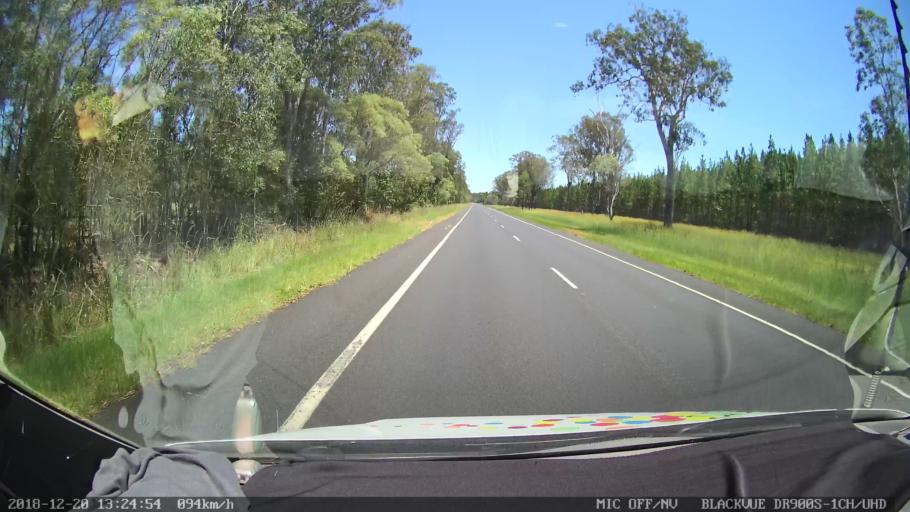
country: AU
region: New South Wales
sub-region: Richmond Valley
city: Casino
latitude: -29.1237
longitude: 152.9985
